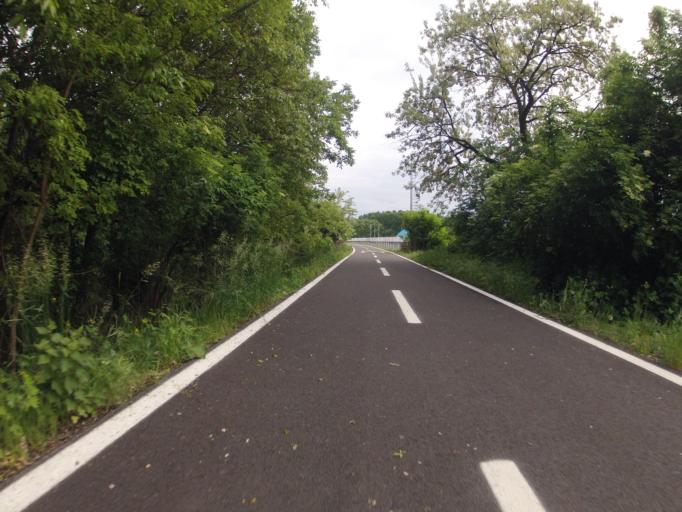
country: IT
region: Piedmont
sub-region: Provincia di Torino
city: Villafranca Piemonte
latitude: 44.7834
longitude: 7.5105
